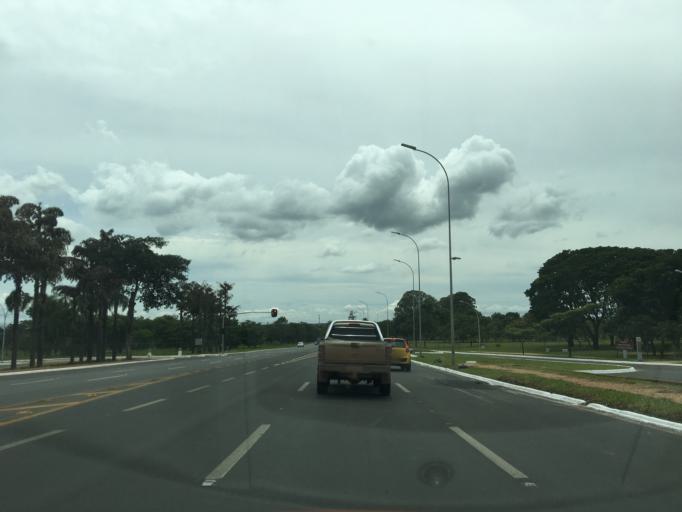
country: BR
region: Federal District
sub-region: Brasilia
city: Brasilia
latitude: -15.8005
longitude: -47.8583
